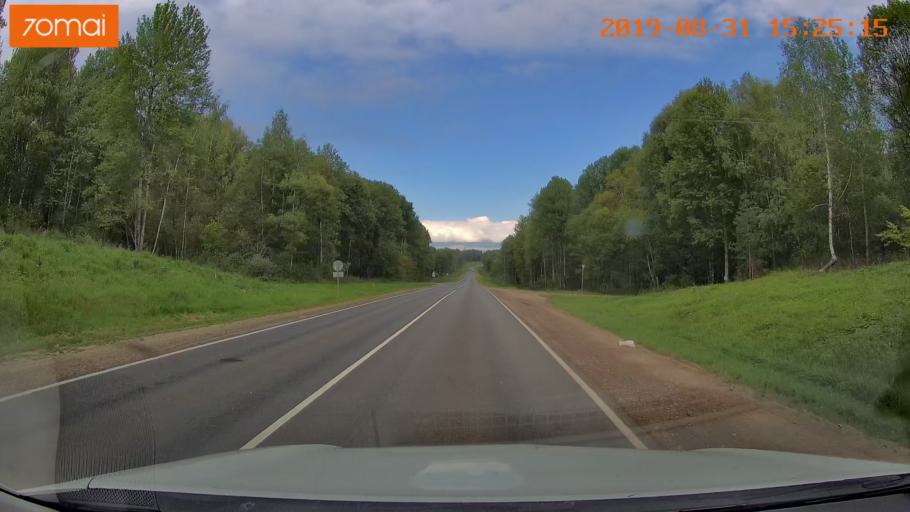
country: RU
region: Kaluga
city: Baryatino
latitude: 54.5389
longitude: 34.5169
